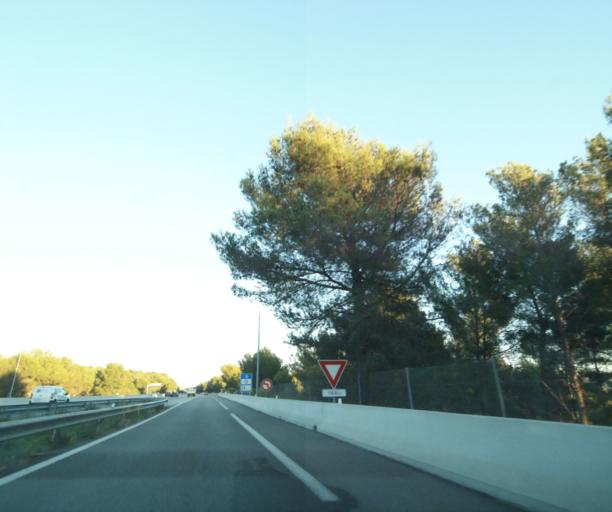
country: FR
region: Provence-Alpes-Cote d'Azur
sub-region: Departement du Var
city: Saint-Cyr-sur-Mer
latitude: 43.1928
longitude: 5.6723
